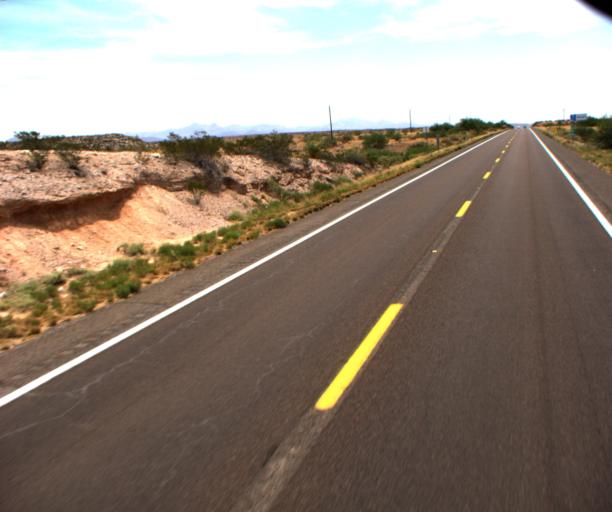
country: US
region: Arizona
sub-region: Graham County
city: Bylas
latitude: 33.2062
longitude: -110.1986
